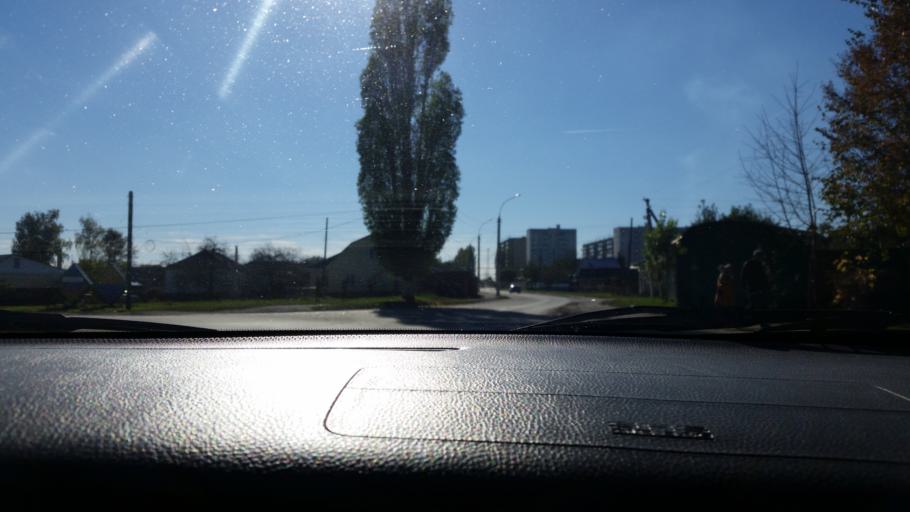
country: RU
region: Lipetsk
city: Gryazi
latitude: 52.4775
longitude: 39.9498
